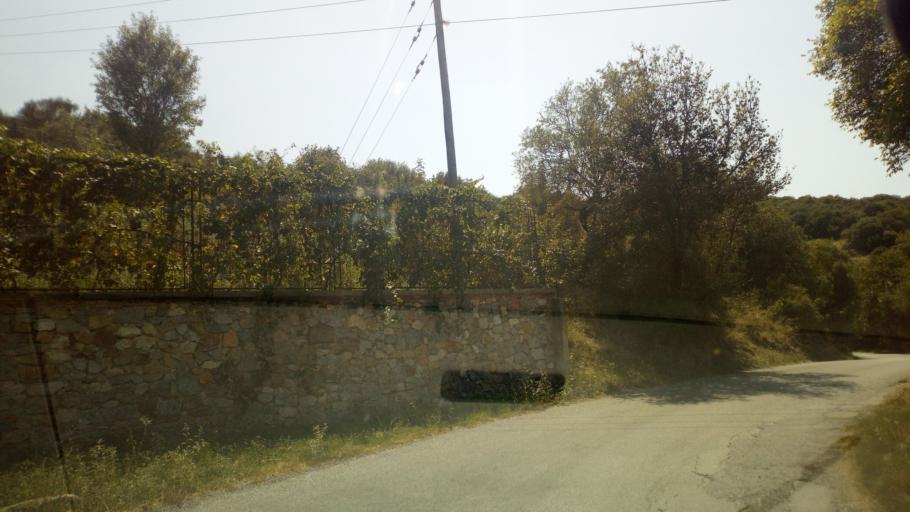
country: GR
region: Central Macedonia
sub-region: Nomos Thessalonikis
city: Asvestochori
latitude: 40.6381
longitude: 23.0162
